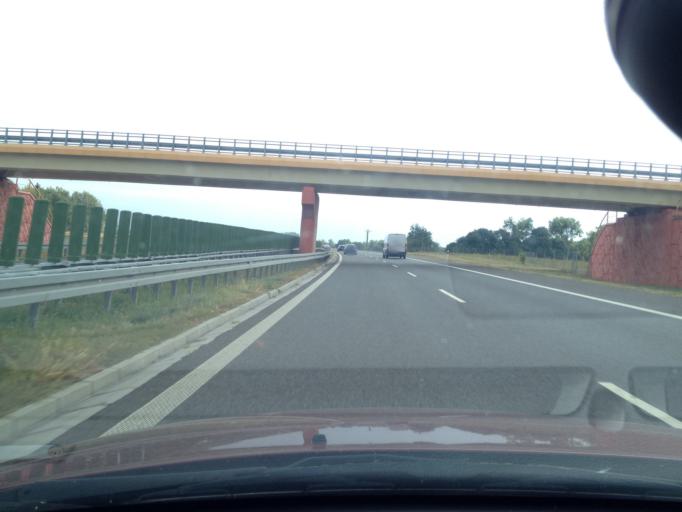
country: PL
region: West Pomeranian Voivodeship
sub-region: Powiat mysliborski
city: Mysliborz
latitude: 52.9950
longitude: 14.8627
